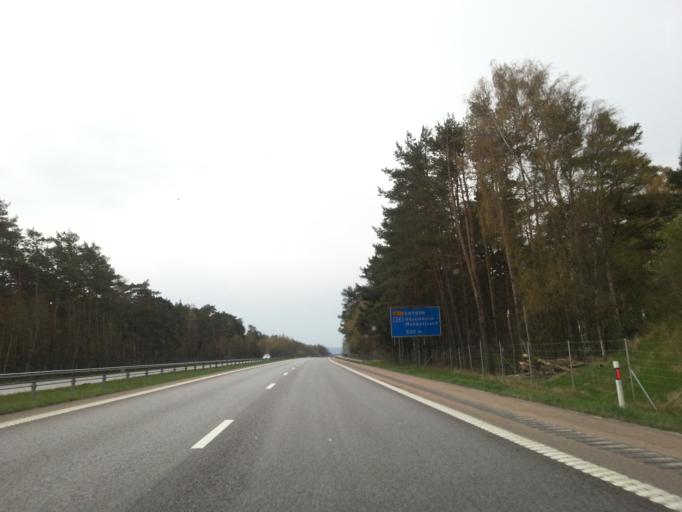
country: SE
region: Halland
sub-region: Laholms Kommun
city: Mellbystrand
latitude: 56.5151
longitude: 12.9643
